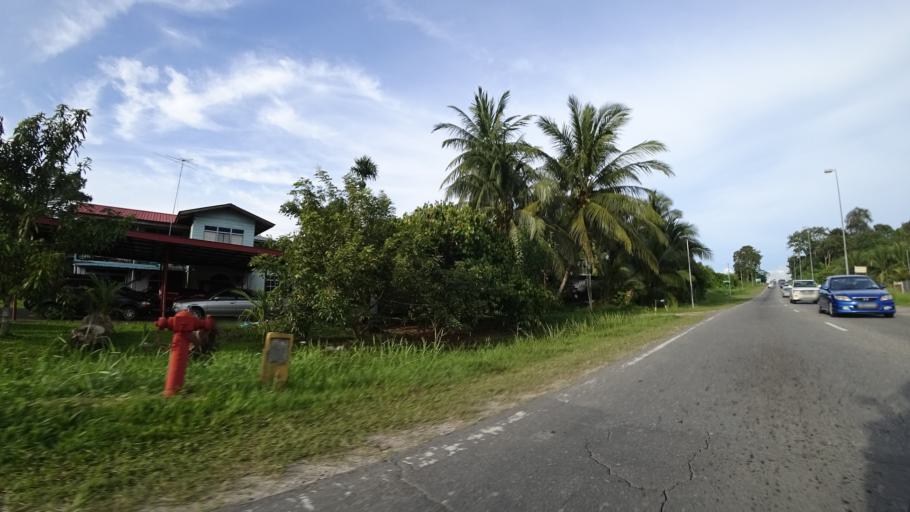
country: BN
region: Brunei and Muara
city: Bandar Seri Begawan
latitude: 4.8831
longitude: 114.8348
